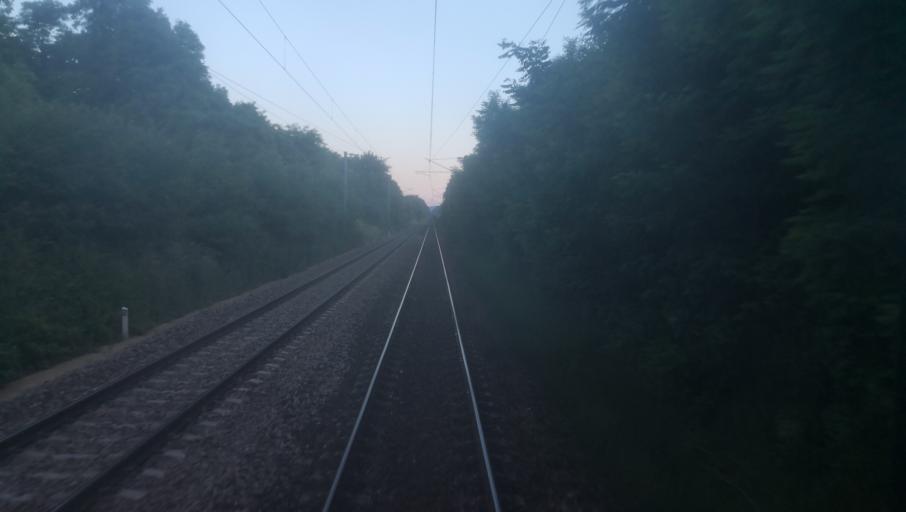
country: FR
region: Bourgogne
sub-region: Departement de la Nievre
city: Cosne-Cours-sur-Loire
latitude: 47.3712
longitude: 2.8991
